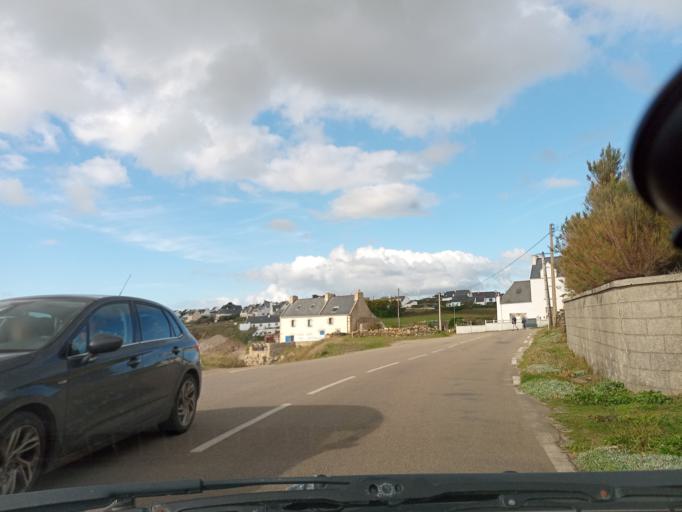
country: FR
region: Brittany
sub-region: Departement du Finistere
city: Plozevet
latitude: 47.9787
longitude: -4.4487
